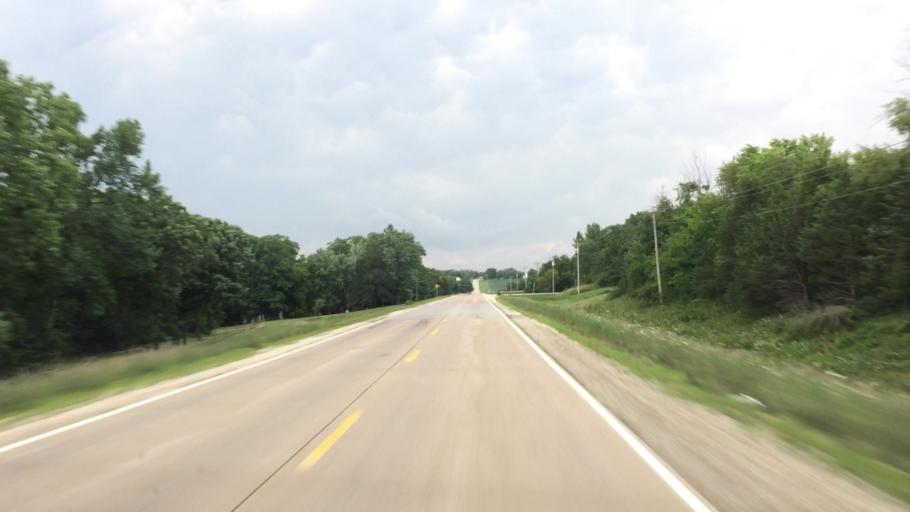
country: US
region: Iowa
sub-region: Lee County
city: Fort Madison
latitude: 40.7163
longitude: -91.3299
